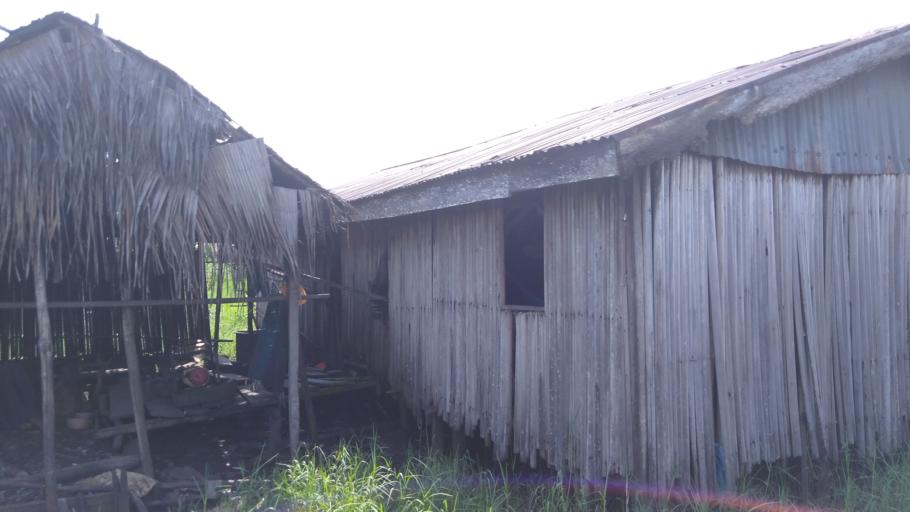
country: NG
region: Ondo
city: Igbekebo
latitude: 5.9224
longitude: 4.9659
